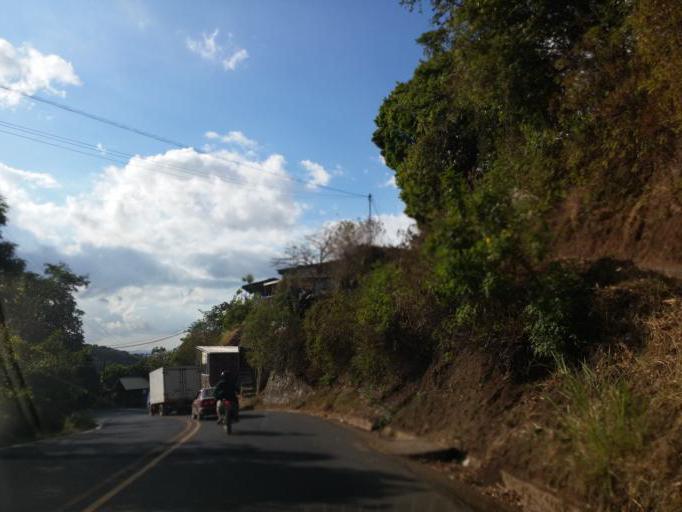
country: CR
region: San Jose
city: San Ignacio
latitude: 9.7950
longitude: -84.1484
